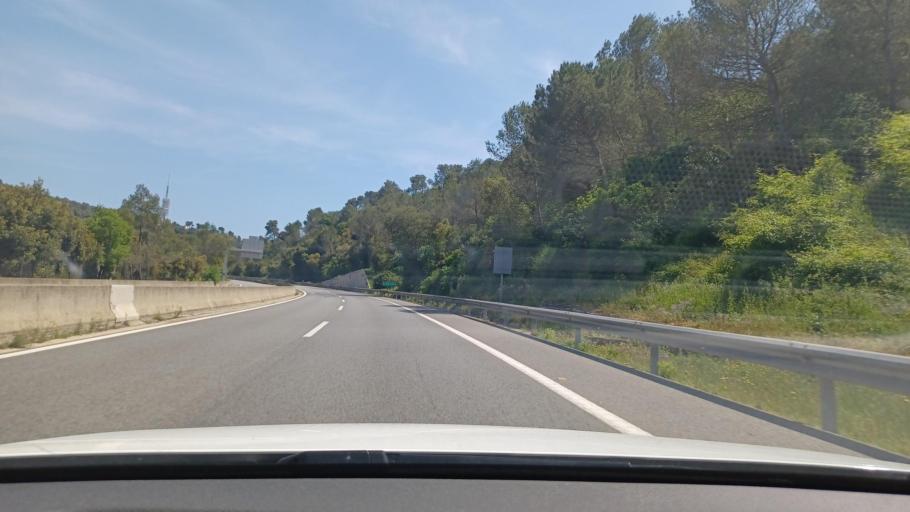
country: ES
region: Catalonia
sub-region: Provincia de Barcelona
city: Sant Cugat del Valles
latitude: 41.4299
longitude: 2.0836
